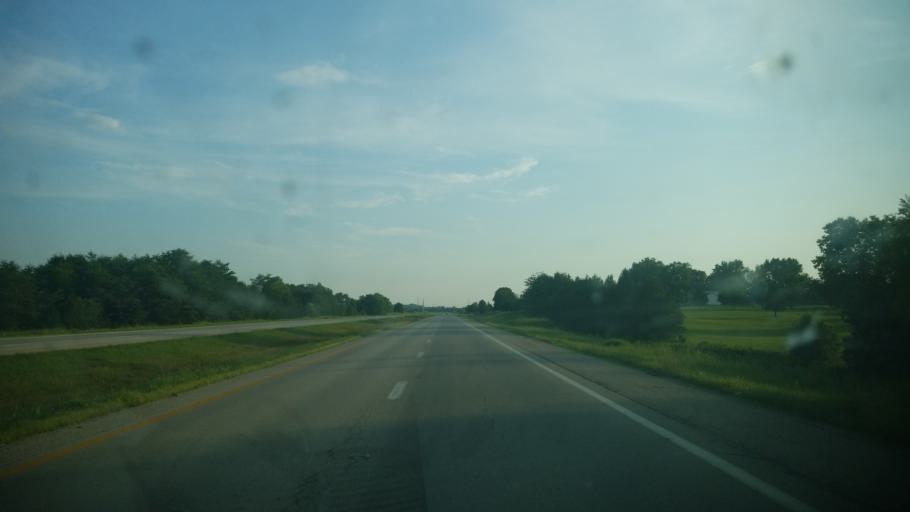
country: US
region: Ohio
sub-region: Adams County
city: Peebles
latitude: 38.9643
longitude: -83.3536
